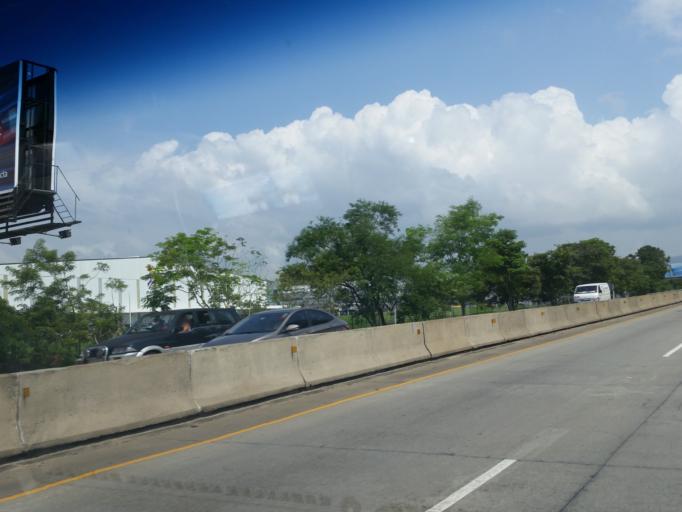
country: PA
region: Panama
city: Tocumen
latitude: 9.0631
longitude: -79.4033
